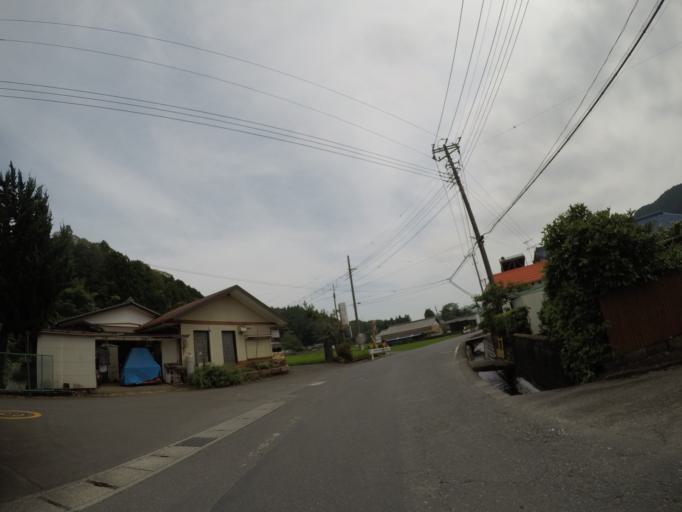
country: JP
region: Shizuoka
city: Fujinomiya
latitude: 35.2235
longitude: 138.5673
